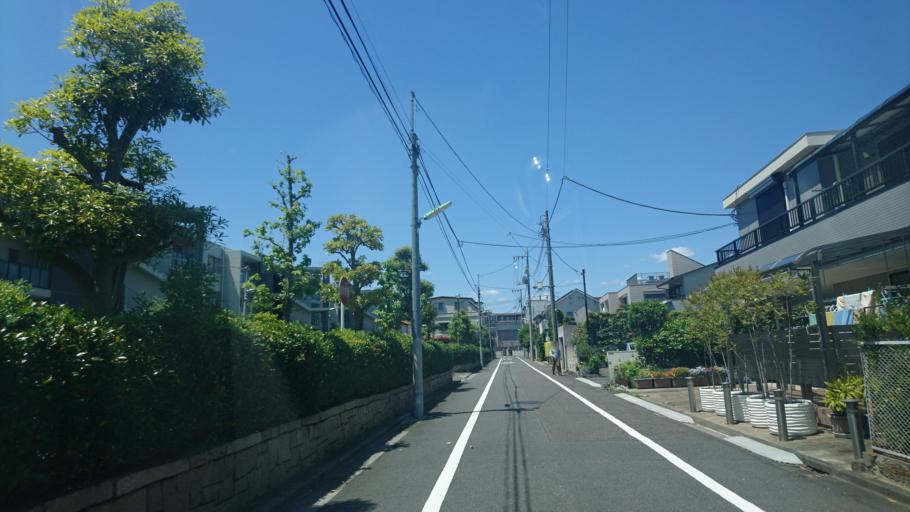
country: JP
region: Tokyo
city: Tokyo
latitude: 35.6472
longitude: 139.6301
